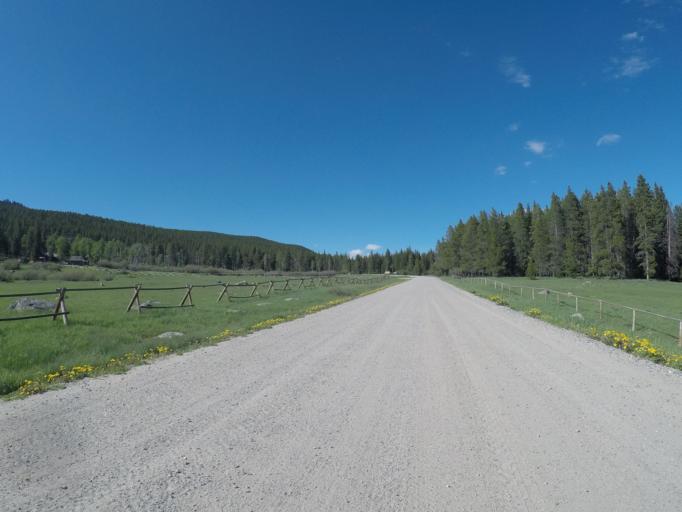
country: US
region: Wyoming
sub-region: Johnson County
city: Buffalo
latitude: 44.1874
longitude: -107.2494
